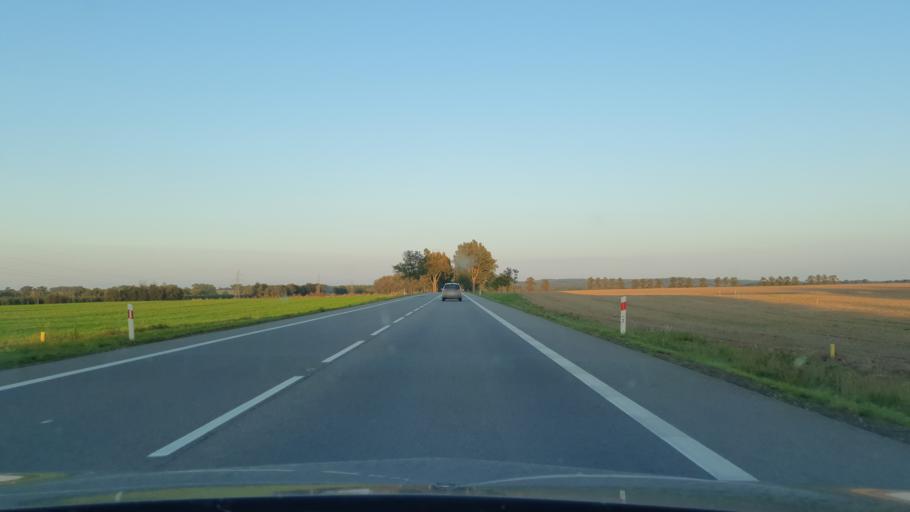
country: PL
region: Pomeranian Voivodeship
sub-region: Powiat slupski
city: Potegowo
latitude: 54.4779
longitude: 17.5267
